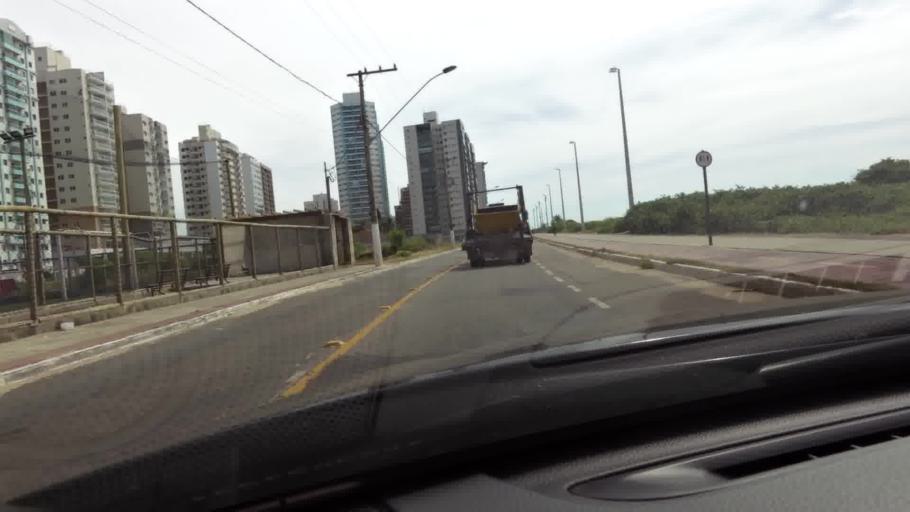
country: BR
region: Espirito Santo
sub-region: Vila Velha
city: Vila Velha
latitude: -20.3805
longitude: -40.3085
